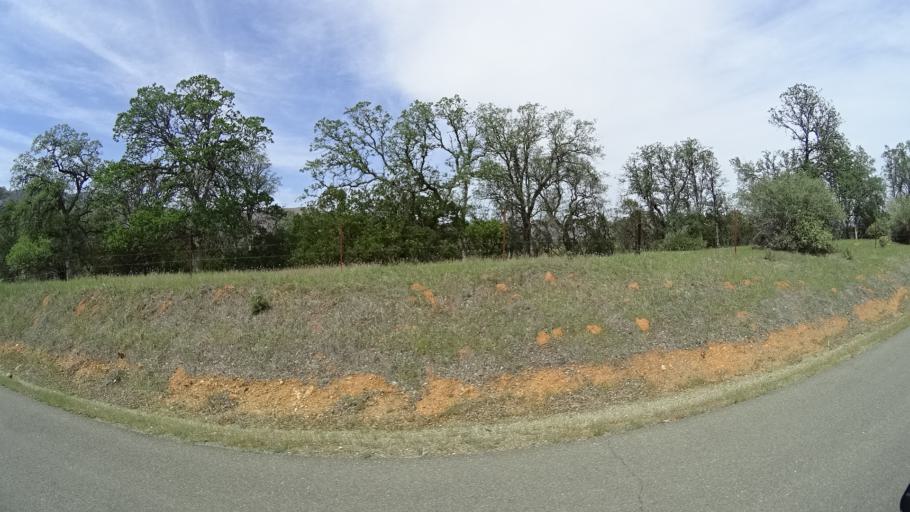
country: US
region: California
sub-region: Glenn County
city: Willows
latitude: 39.5831
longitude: -122.5929
